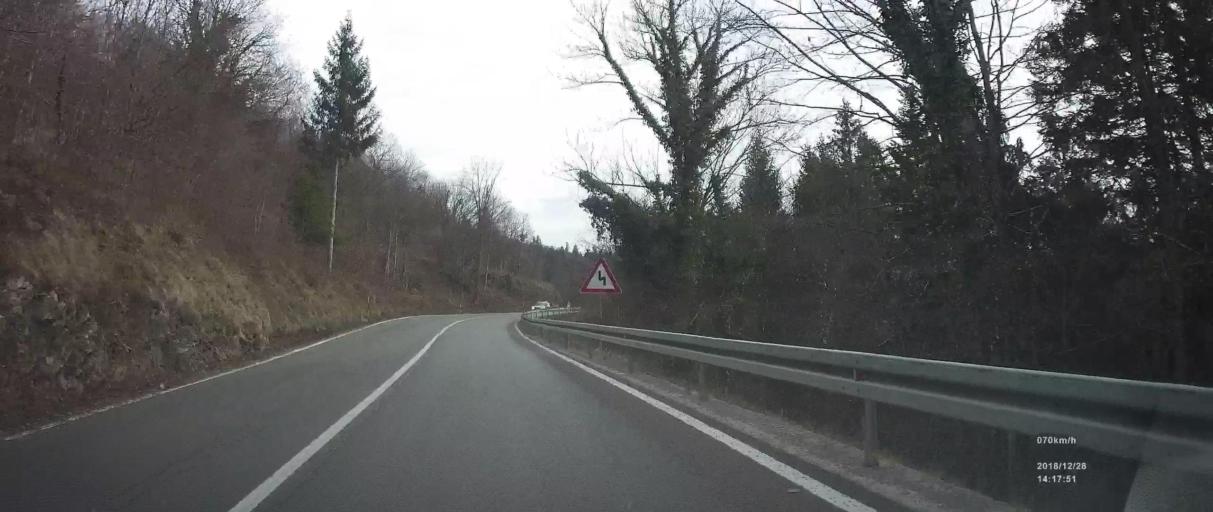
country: HR
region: Primorsko-Goranska
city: Vrbovsko
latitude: 45.4172
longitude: 15.0546
